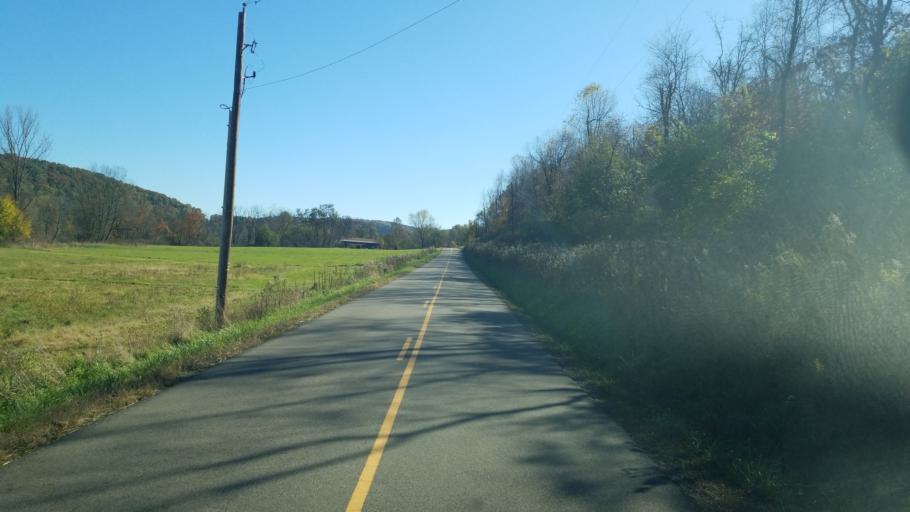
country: US
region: Ohio
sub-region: Knox County
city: Danville
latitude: 40.5287
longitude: -82.2026
